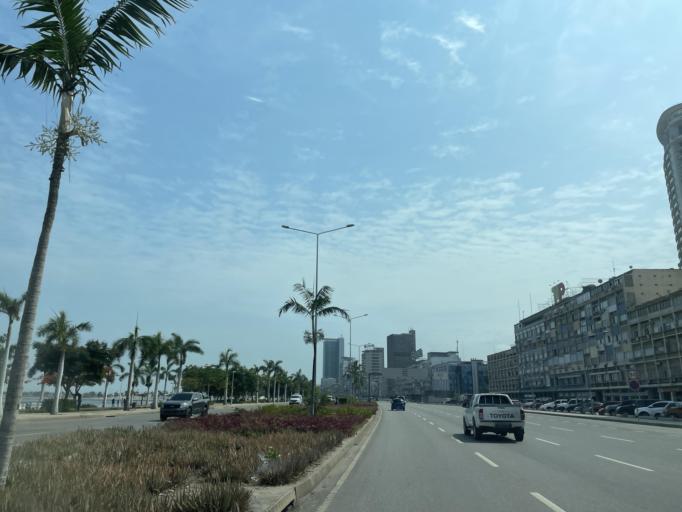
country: AO
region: Luanda
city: Luanda
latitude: -8.8088
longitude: 13.2369
